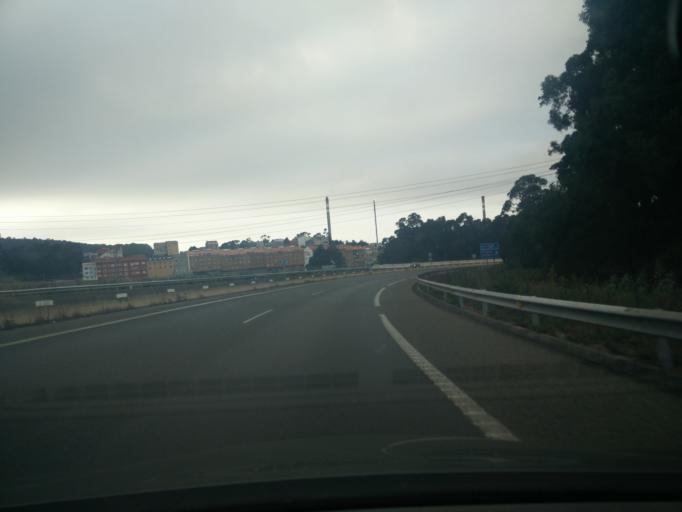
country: ES
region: Galicia
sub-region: Provincia da Coruna
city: Arteixo
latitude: 43.3364
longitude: -8.4552
